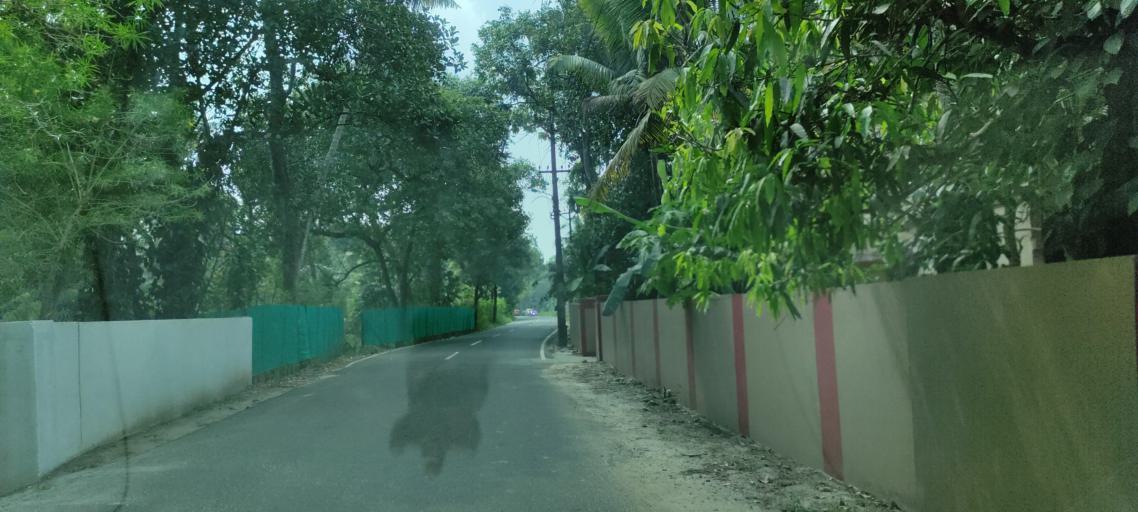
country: IN
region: Kerala
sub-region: Alappuzha
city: Shertallai
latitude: 9.6034
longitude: 76.3429
